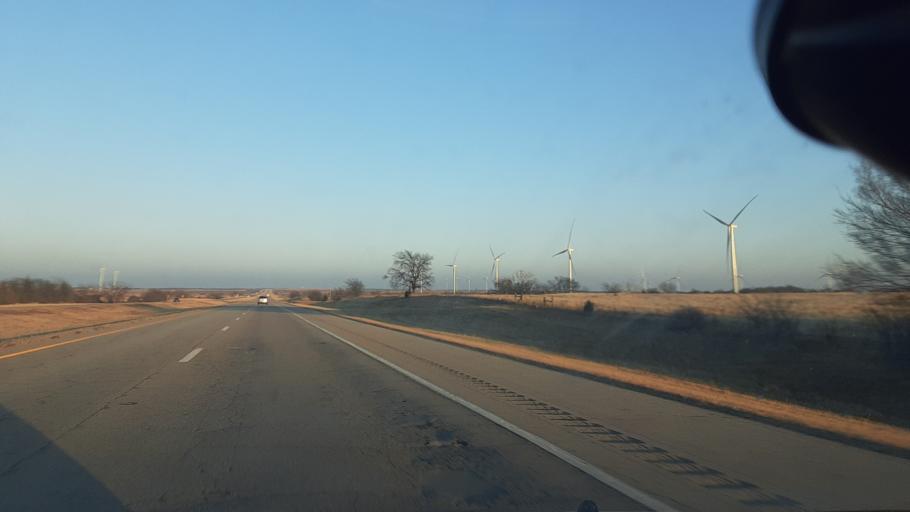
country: US
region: Oklahoma
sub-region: Noble County
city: Perry
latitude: 36.3978
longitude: -97.4301
